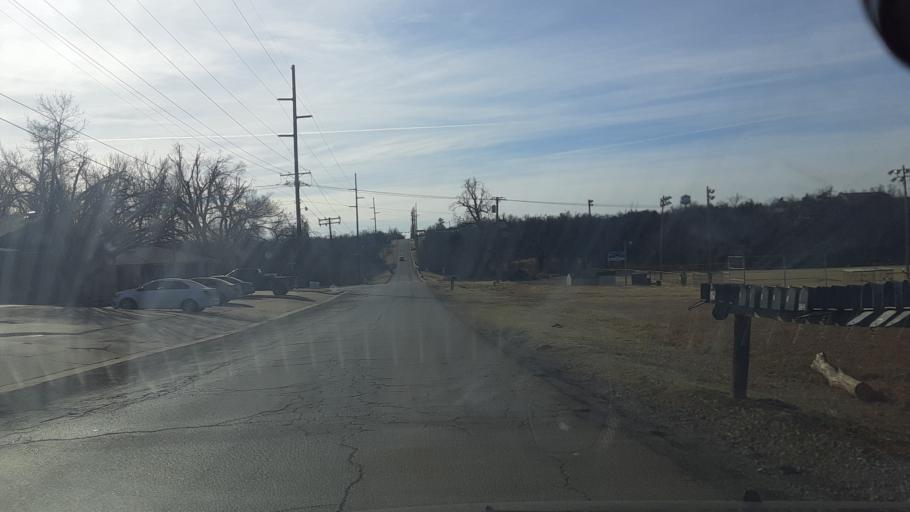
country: US
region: Oklahoma
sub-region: Logan County
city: Guthrie
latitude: 35.8860
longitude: -97.4076
